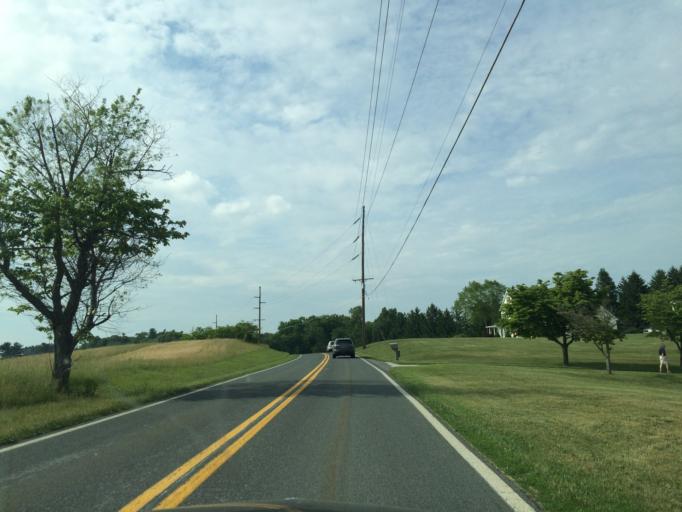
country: US
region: Maryland
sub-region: Baltimore County
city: Reisterstown
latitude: 39.4629
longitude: -76.8976
